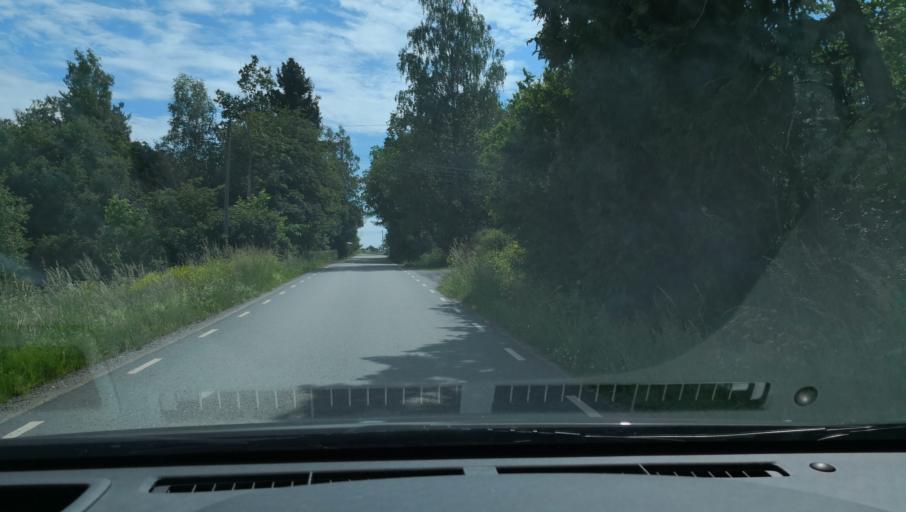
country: SE
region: Uppsala
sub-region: Habo Kommun
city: Balsta
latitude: 59.6814
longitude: 17.4656
